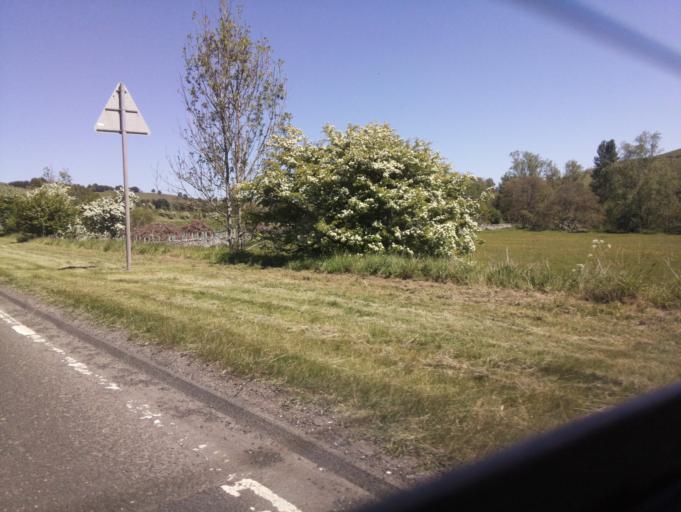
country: GB
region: Scotland
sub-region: The Scottish Borders
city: Selkirk
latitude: 55.4947
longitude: -2.8352
